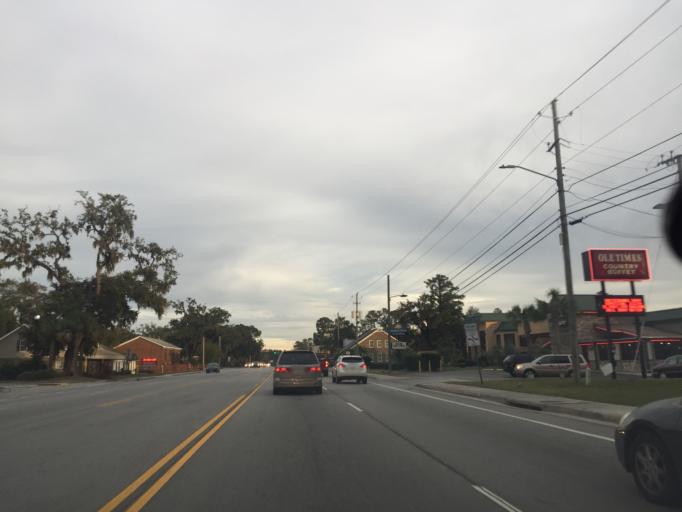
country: US
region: Georgia
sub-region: Chatham County
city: Isle of Hope
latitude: 32.0131
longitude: -81.1107
